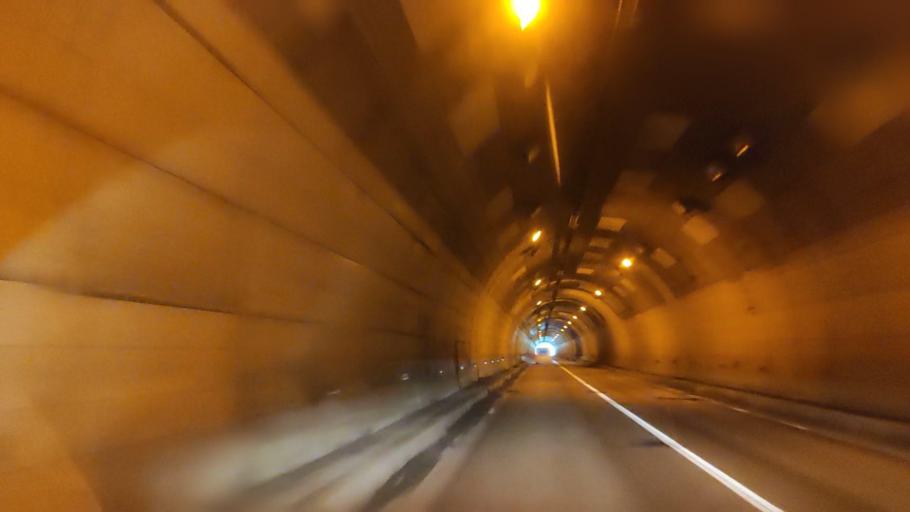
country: JP
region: Hokkaido
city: Bibai
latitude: 43.2888
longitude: 142.0728
